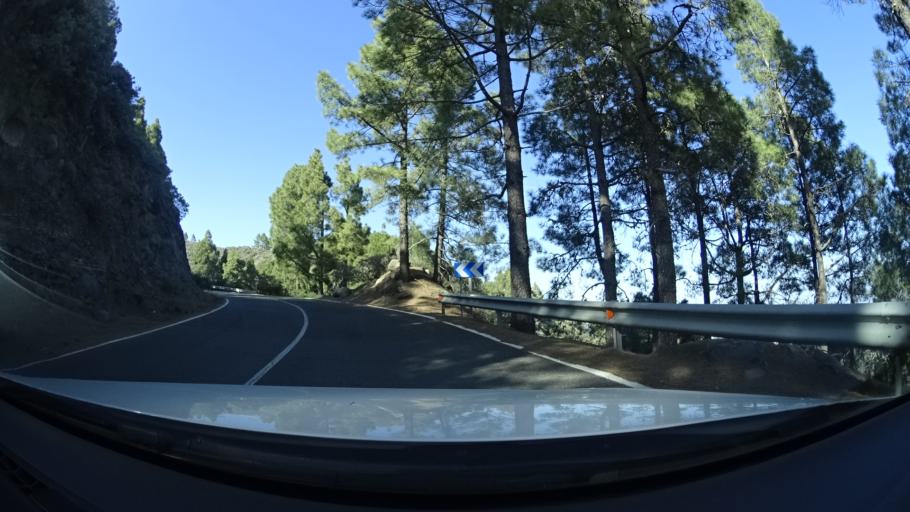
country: ES
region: Canary Islands
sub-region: Provincia de Las Palmas
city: Valsequillo de Gran Canaria
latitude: 27.9625
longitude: -15.5375
